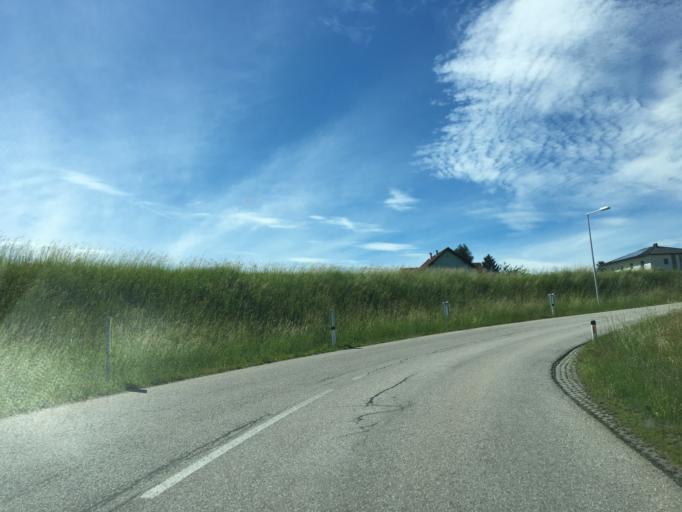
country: AT
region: Upper Austria
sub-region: Politischer Bezirk Urfahr-Umgebung
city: Bad Leonfelden
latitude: 48.5145
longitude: 14.2950
